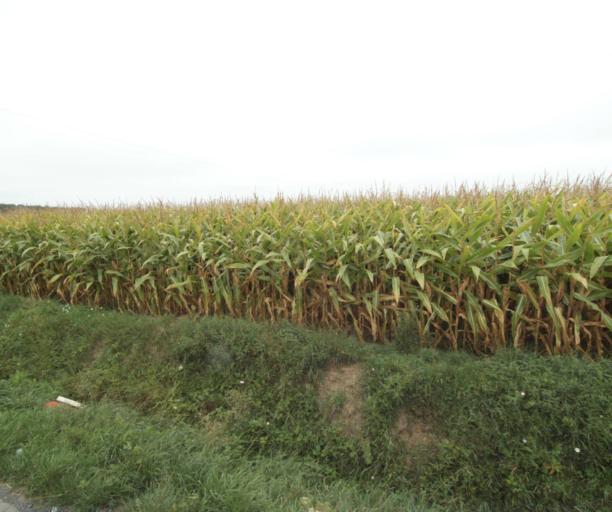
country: FR
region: Nord-Pas-de-Calais
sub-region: Departement du Nord
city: Sailly-lez-Lannoy
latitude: 50.6375
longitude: 3.2126
